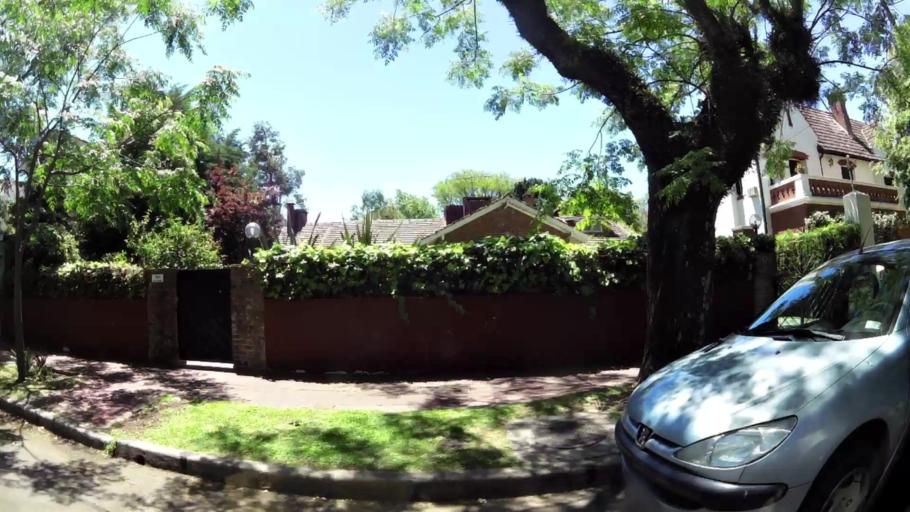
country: AR
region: Buenos Aires
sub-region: Partido de San Isidro
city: San Isidro
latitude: -34.4750
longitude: -58.5054
